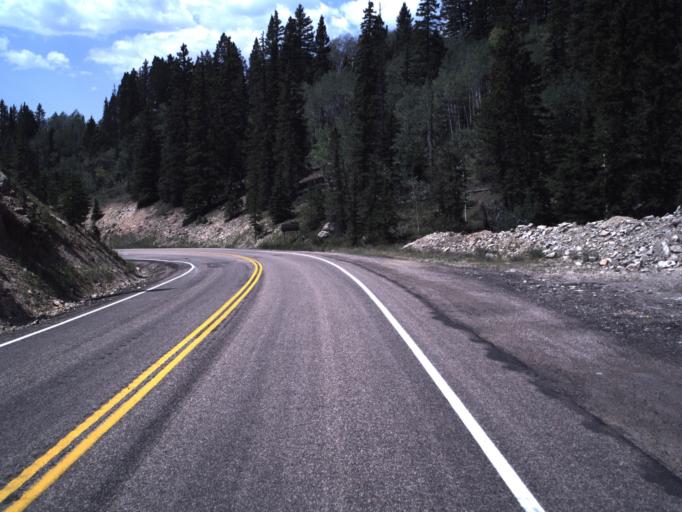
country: US
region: Utah
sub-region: Uintah County
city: Maeser
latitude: 40.7123
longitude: -109.4926
